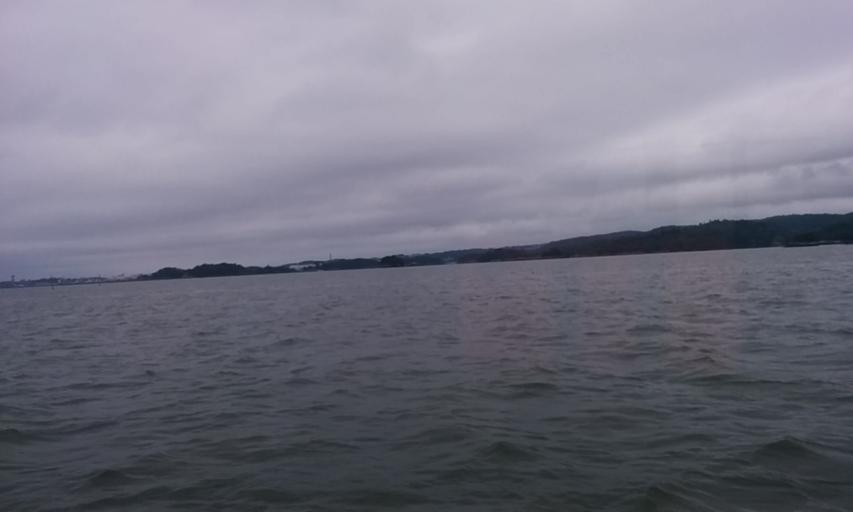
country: JP
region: Miyagi
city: Matsushima
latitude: 38.3495
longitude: 141.0750
